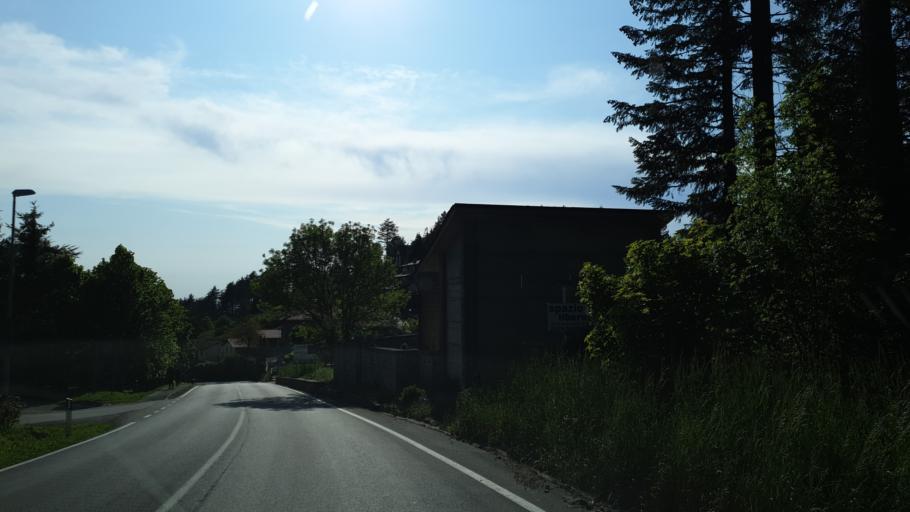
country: IT
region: Tuscany
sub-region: Province of Arezzo
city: Montemignaio
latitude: 43.7830
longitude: 11.6009
